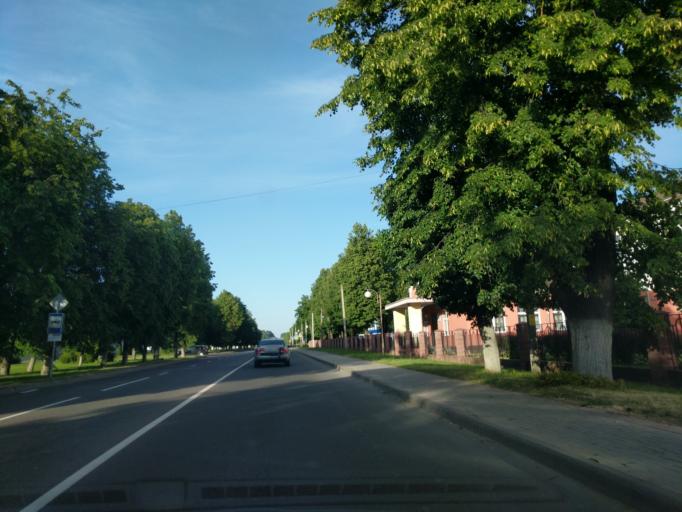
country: BY
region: Grodnenskaya
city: Ashmyany
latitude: 54.4320
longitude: 25.9578
